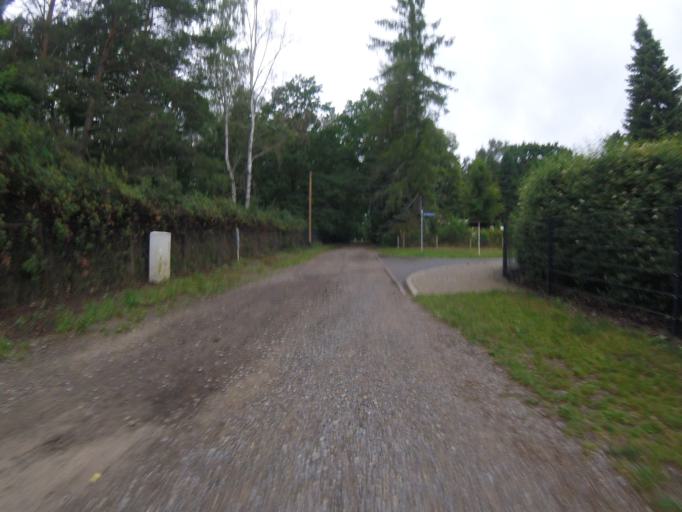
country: DE
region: Brandenburg
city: Bestensee
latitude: 52.2631
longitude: 13.6135
